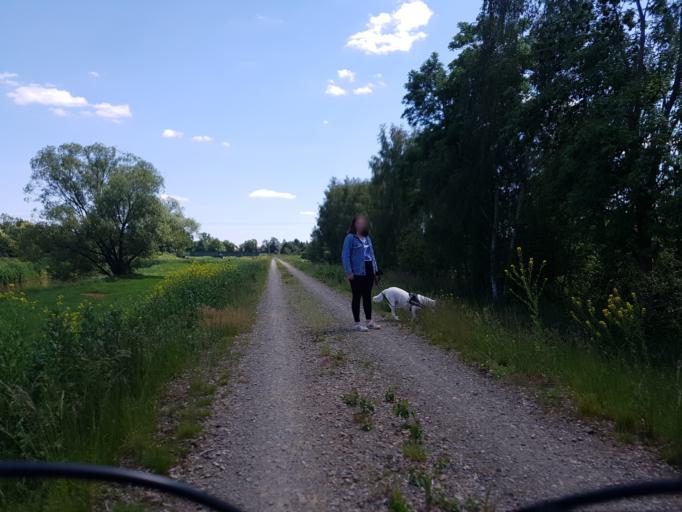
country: DE
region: Brandenburg
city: Bad Liebenwerda
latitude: 51.5239
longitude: 13.3858
